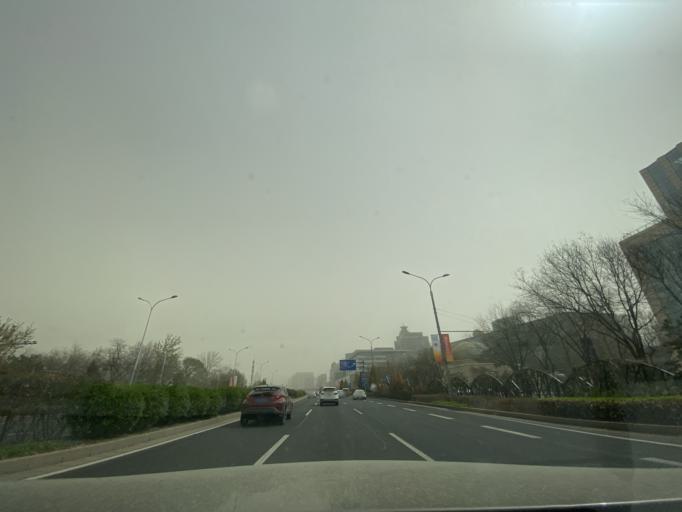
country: CN
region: Beijing
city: Jinrongjie
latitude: 39.9368
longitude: 116.3285
